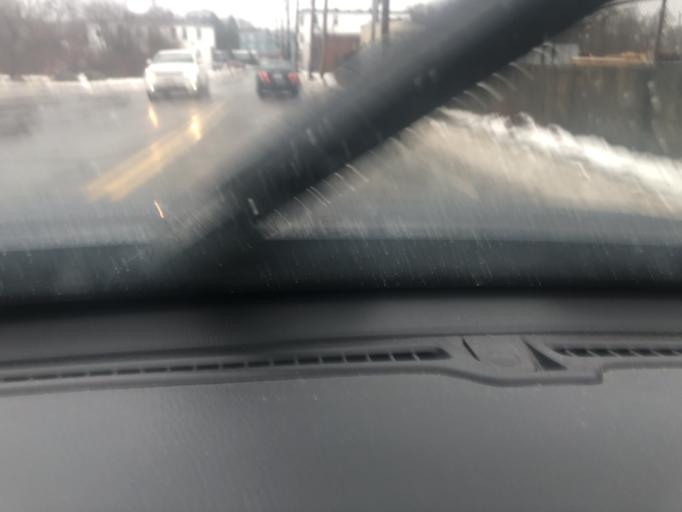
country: US
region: Massachusetts
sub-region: Plymouth County
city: Brockton
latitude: 42.1022
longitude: -71.0180
